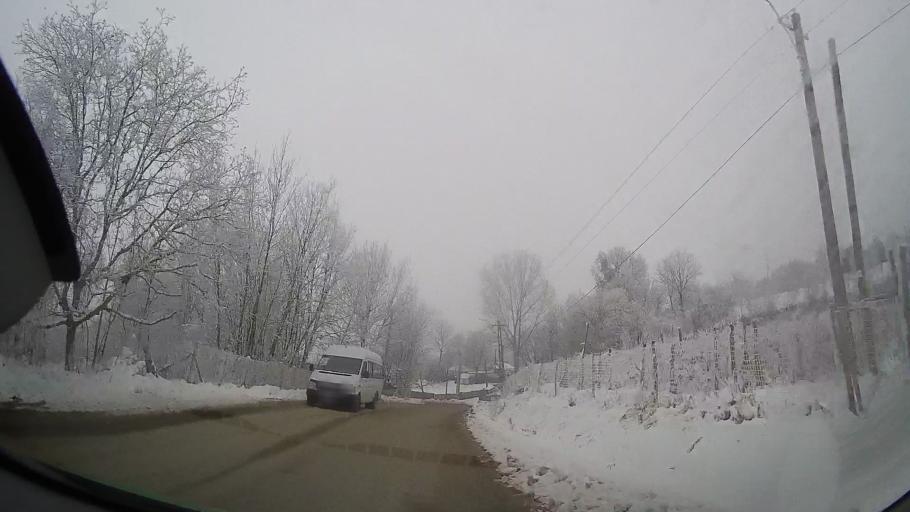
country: RO
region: Iasi
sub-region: Comuna Tansa
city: Tansa
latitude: 46.9114
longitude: 27.2257
